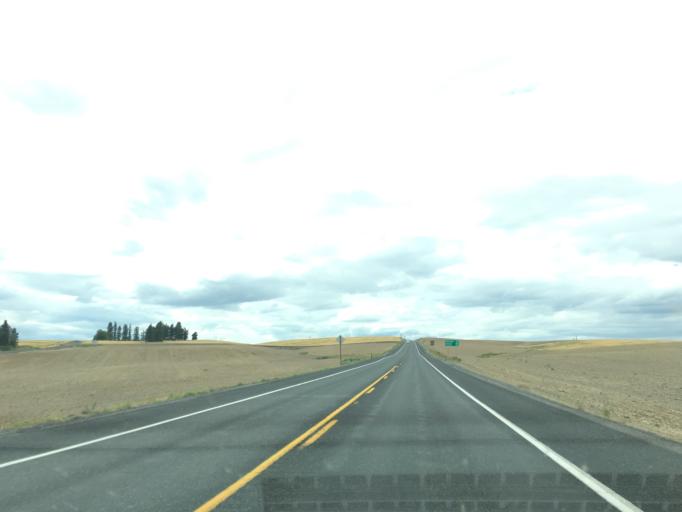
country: US
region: Washington
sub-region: Douglas County
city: Waterville
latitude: 47.6423
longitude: -120.0851
